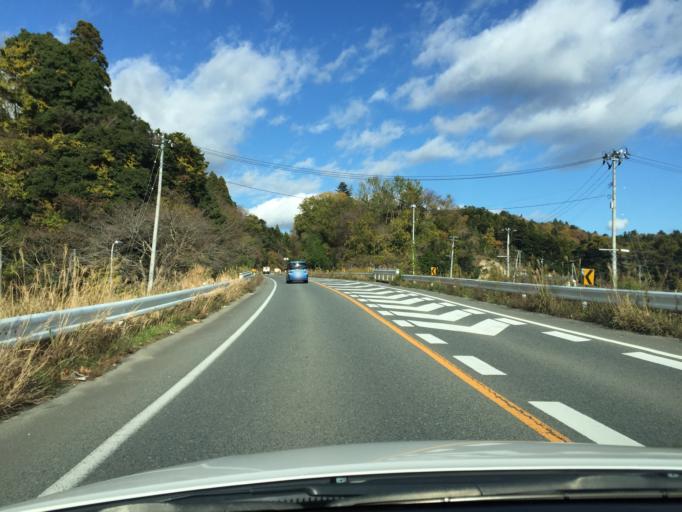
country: JP
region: Fukushima
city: Namie
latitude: 37.5300
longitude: 141.0029
